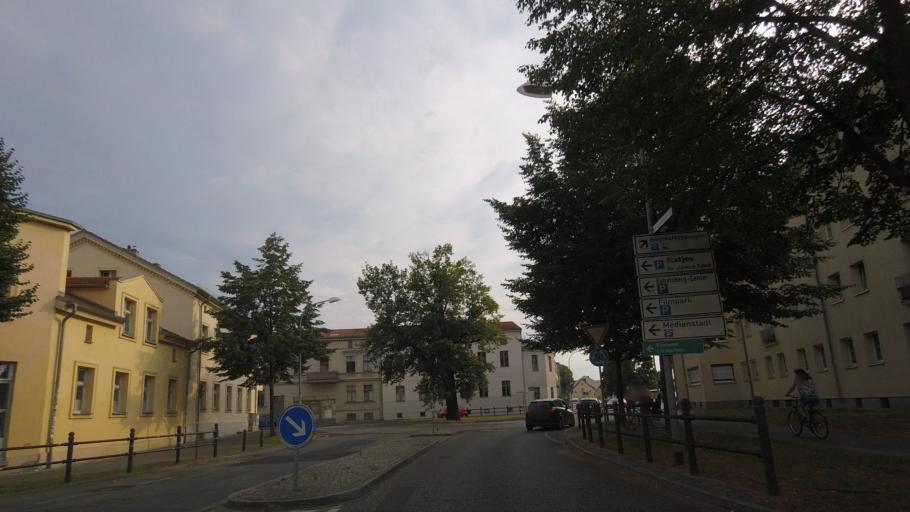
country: DE
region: Brandenburg
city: Potsdam
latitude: 52.3905
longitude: 13.0904
